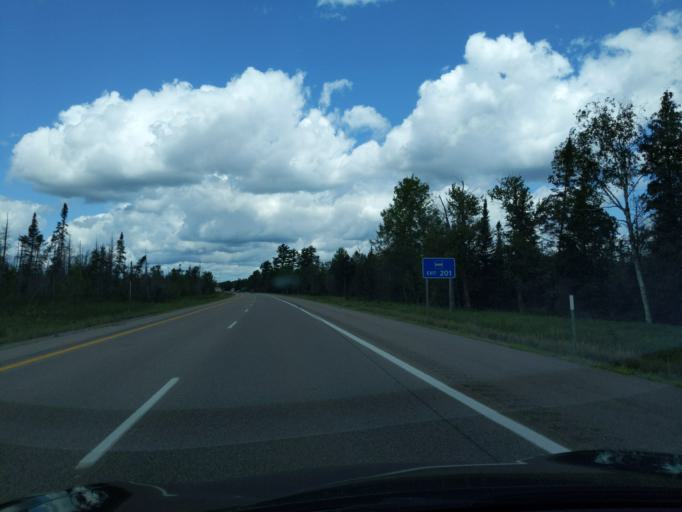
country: US
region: Michigan
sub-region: Roscommon County
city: Houghton Lake
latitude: 44.4233
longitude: -84.7889
